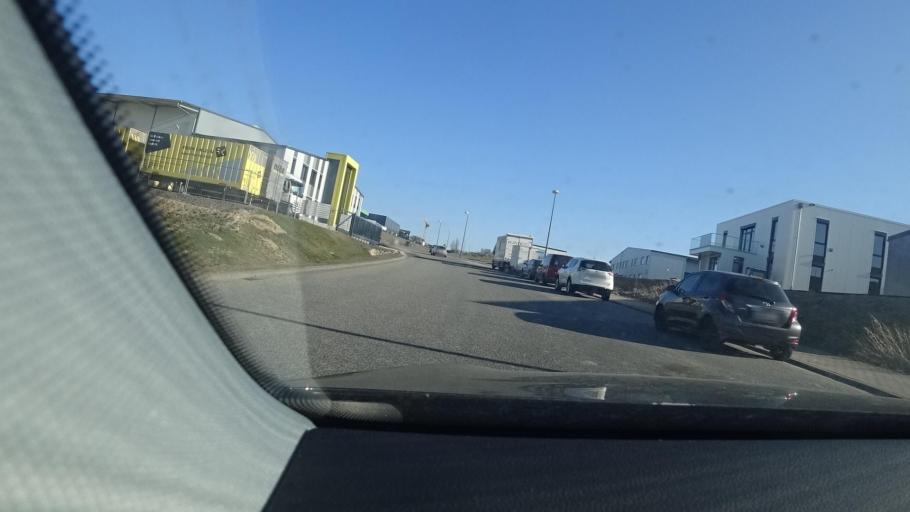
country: DE
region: Rheinland-Pfalz
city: Riesweiler
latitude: 49.9706
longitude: 7.5563
